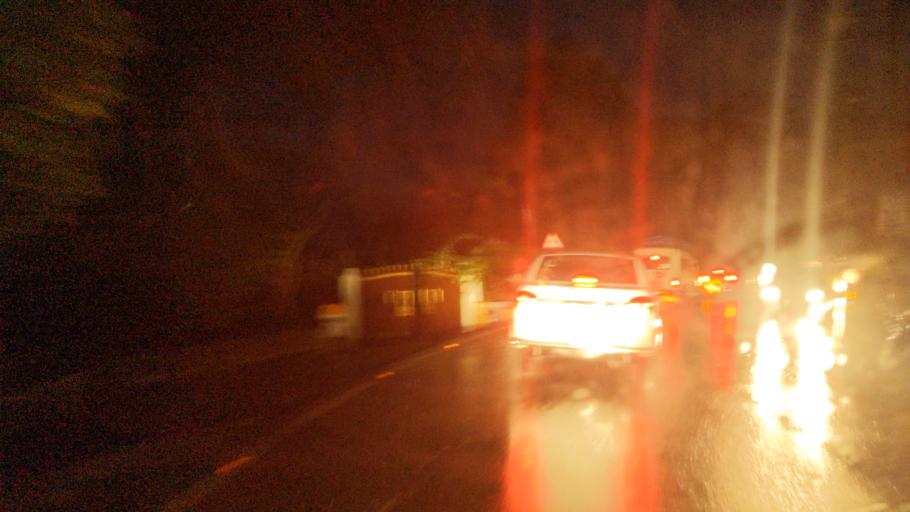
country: IN
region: Uttarakhand
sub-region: Naini Tal
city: Haldwani
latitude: 29.2772
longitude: 79.5458
